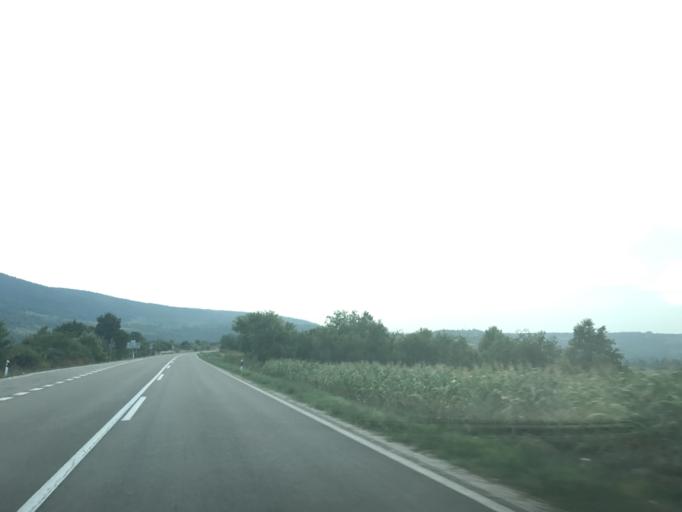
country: RS
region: Central Serbia
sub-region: Zajecarski Okrug
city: Boljevac
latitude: 43.8013
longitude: 21.7747
